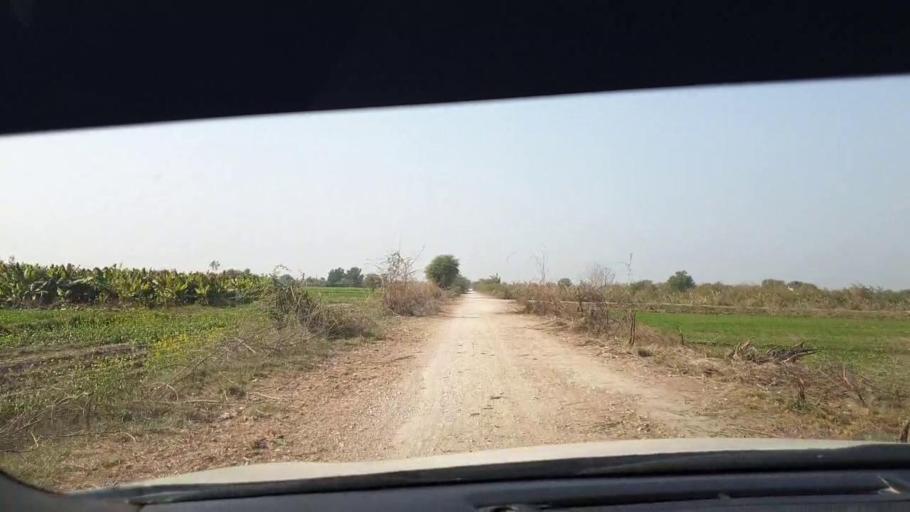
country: PK
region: Sindh
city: Tando Adam
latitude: 25.8413
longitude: 68.7123
